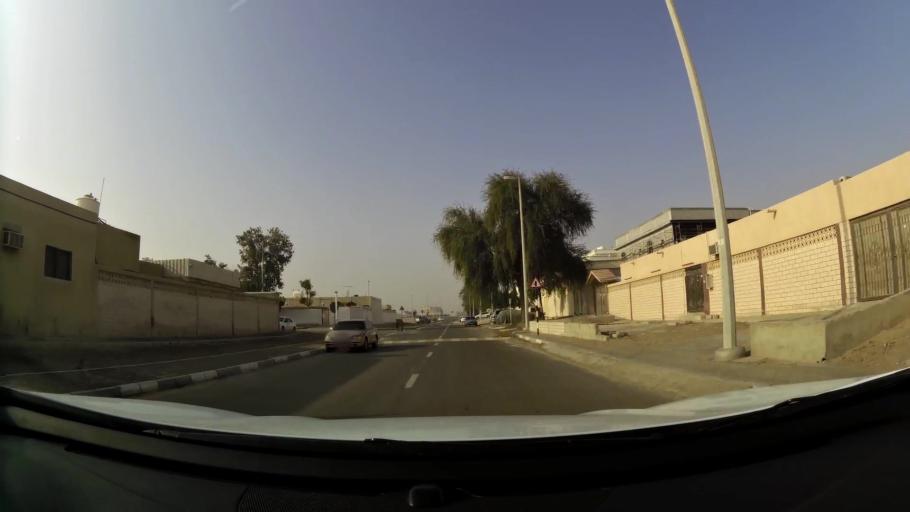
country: AE
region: Abu Dhabi
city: Abu Dhabi
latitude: 24.2763
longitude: 54.6457
